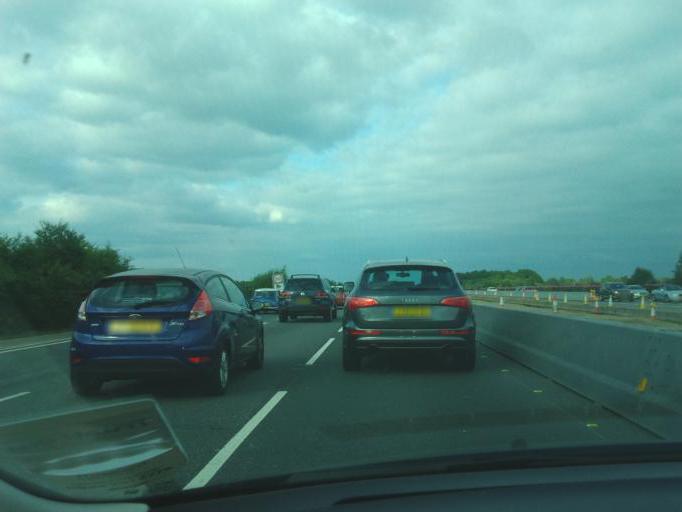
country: GB
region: England
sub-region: Surrey
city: Chobham
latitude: 51.3720
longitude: -0.6142
